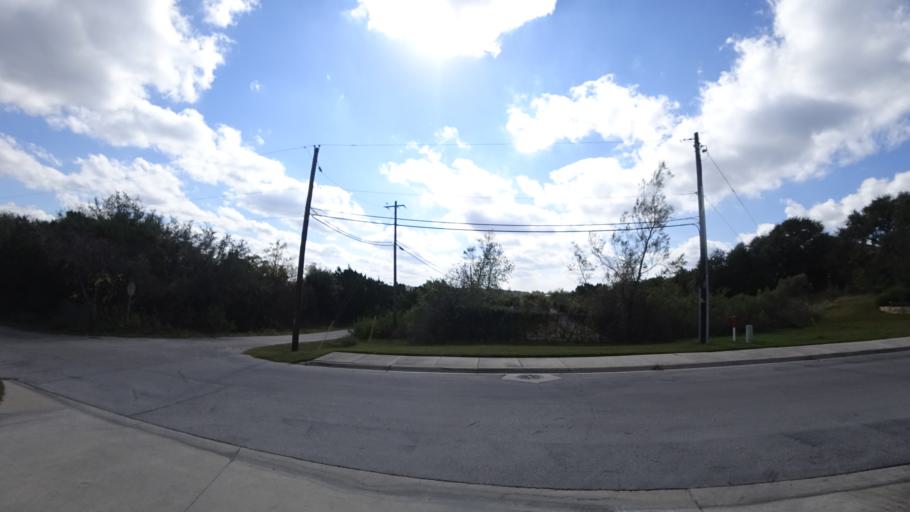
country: US
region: Texas
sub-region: Travis County
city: Barton Creek
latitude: 30.2586
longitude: -97.8908
